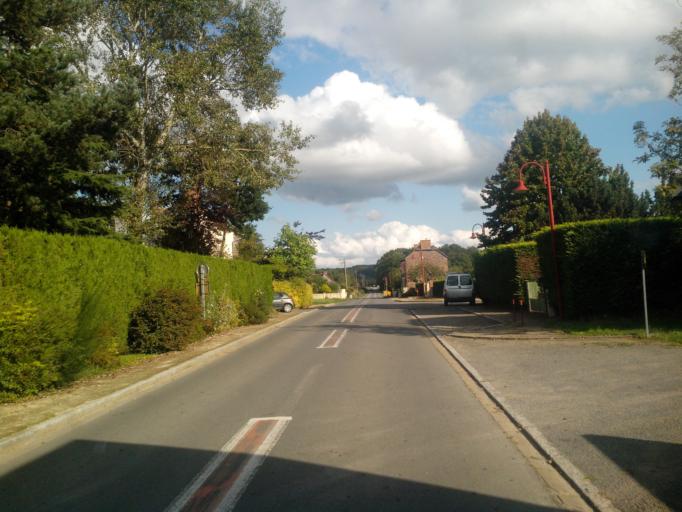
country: FR
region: Brittany
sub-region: Departement d'Ille-et-Vilaine
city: Iffendic
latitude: 48.1130
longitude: -2.0650
